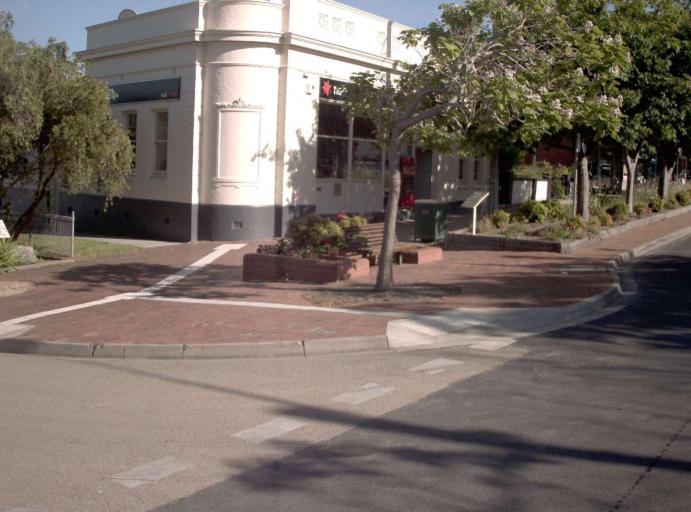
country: AU
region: Victoria
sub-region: East Gippsland
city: Lakes Entrance
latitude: -37.7073
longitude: 148.4549
